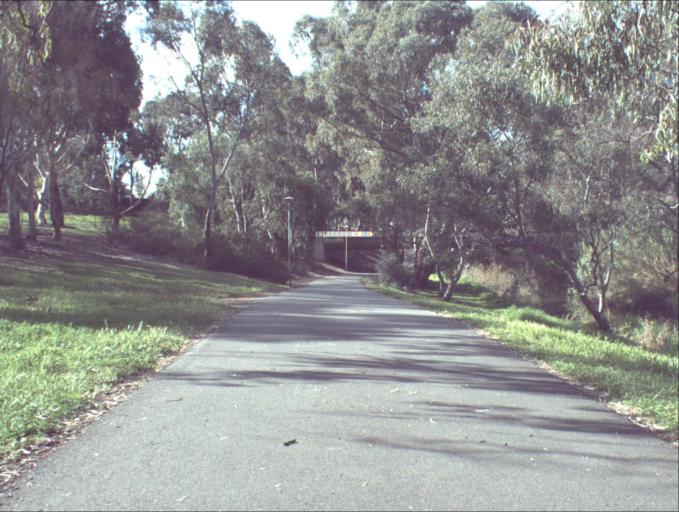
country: AU
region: South Australia
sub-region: Port Adelaide Enfield
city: Klemzig
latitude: -34.8833
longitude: 138.6472
